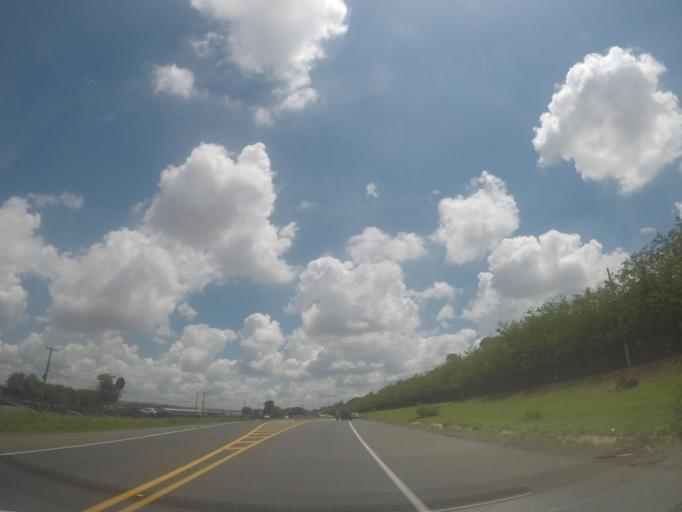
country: BR
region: Sao Paulo
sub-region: Hortolandia
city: Hortolandia
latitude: -22.8329
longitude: -47.2046
